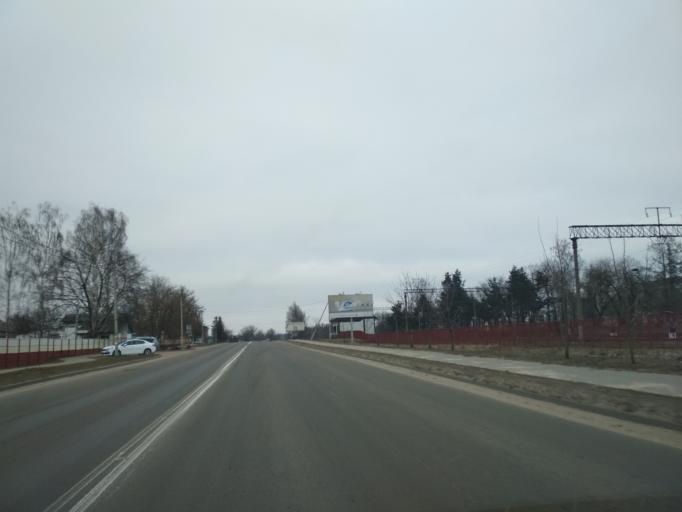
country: BY
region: Minsk
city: Mar''ina Horka
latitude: 53.5135
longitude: 28.1402
